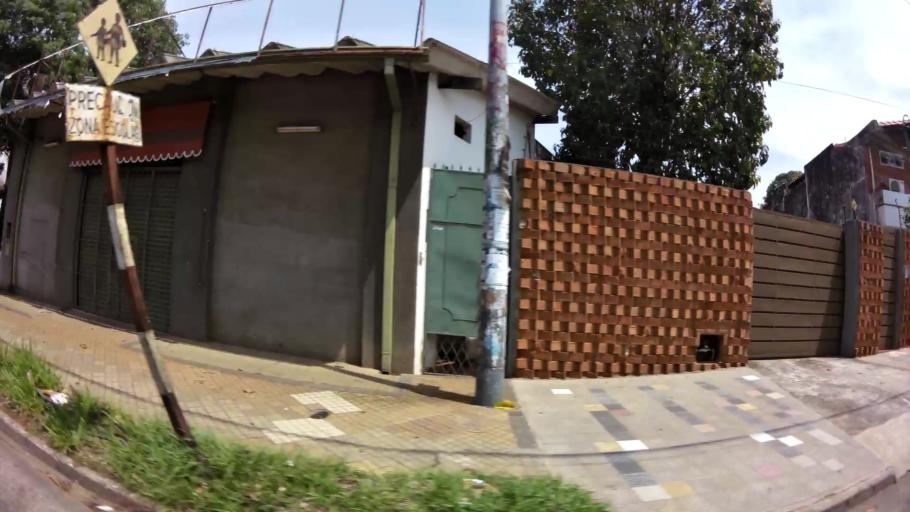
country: PY
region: Central
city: Lambare
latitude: -25.3159
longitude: -57.5986
